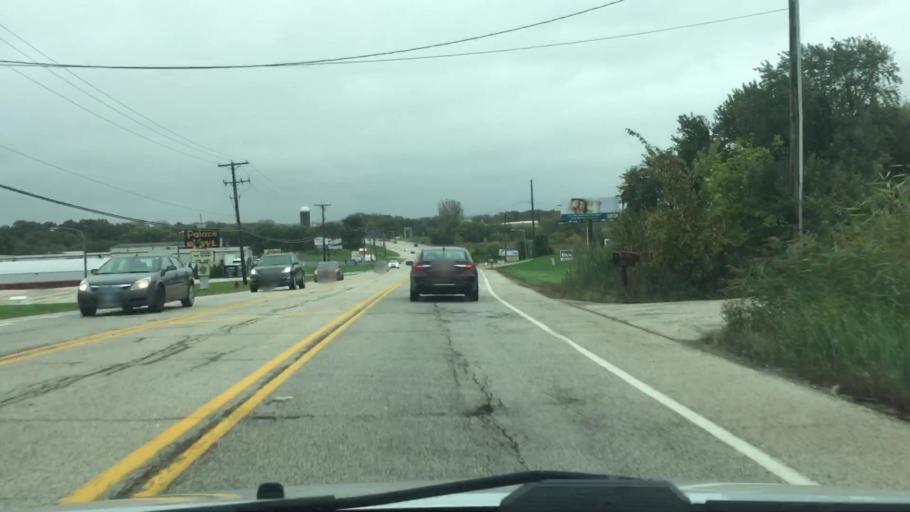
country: US
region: Illinois
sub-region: McHenry County
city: McCullom Lake
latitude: 42.3773
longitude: -88.2693
